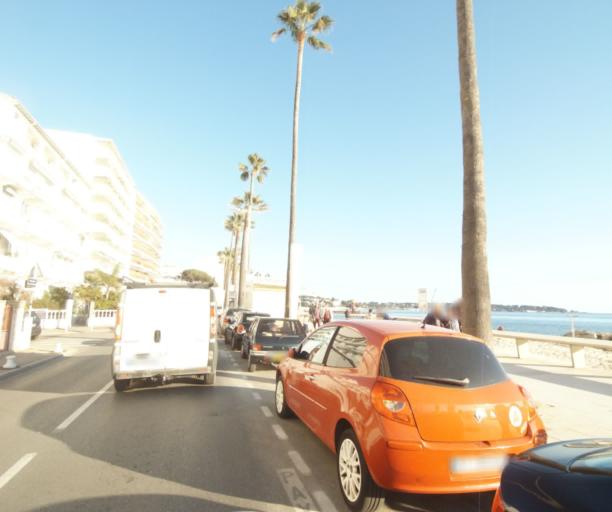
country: FR
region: Provence-Alpes-Cote d'Azur
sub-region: Departement des Alpes-Maritimes
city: Antibes
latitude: 43.5706
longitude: 7.1036
